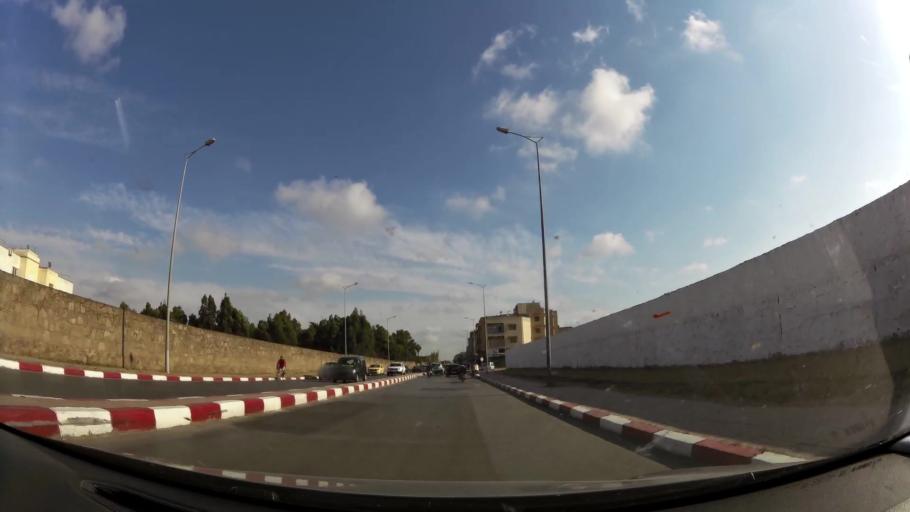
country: MA
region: Rabat-Sale-Zemmour-Zaer
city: Sale
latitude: 34.0497
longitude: -6.7741
